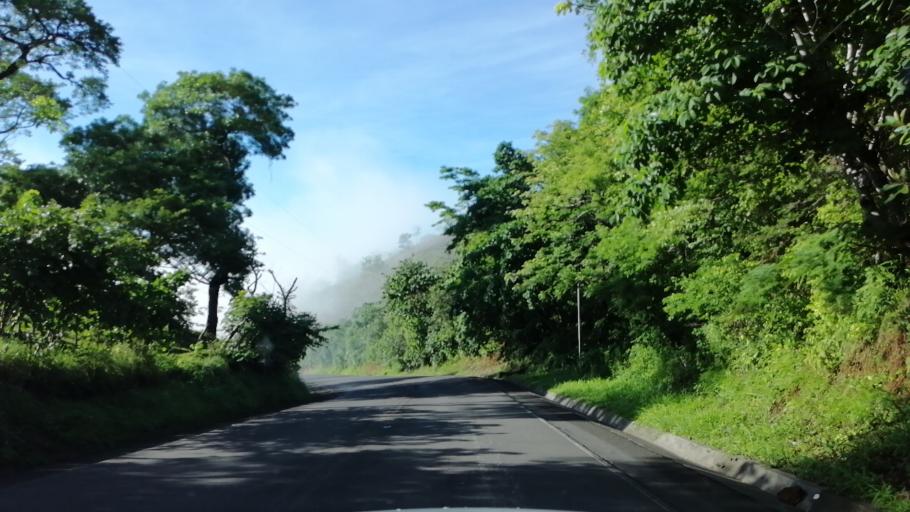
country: SV
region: Morazan
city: Cacaopera
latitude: 13.7925
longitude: -88.1221
